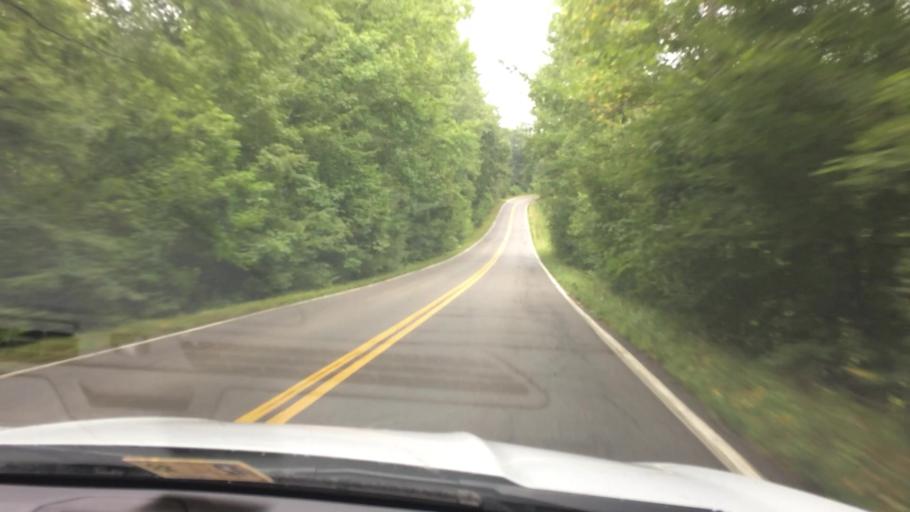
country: US
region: Virginia
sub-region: King William County
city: West Point
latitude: 37.5337
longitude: -76.7478
